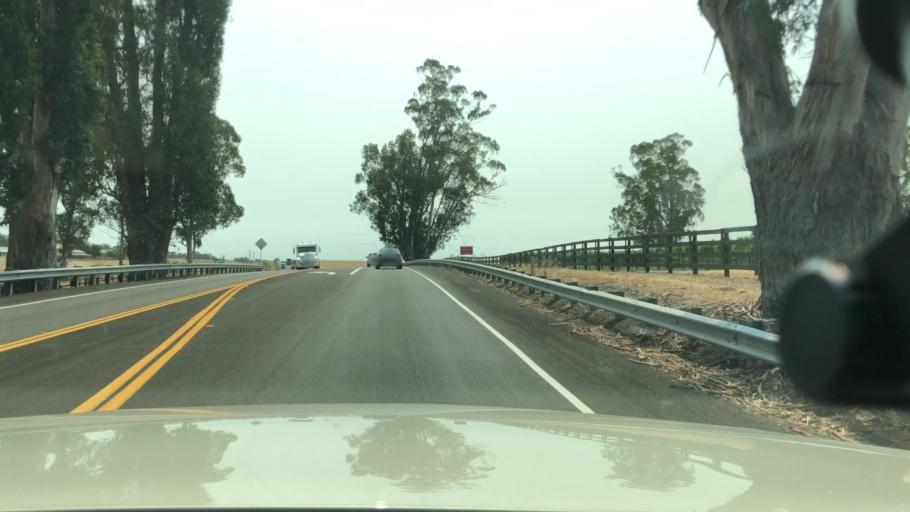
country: US
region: California
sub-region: Marin County
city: Black Point-Green Point
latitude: 38.1743
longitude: -122.5245
